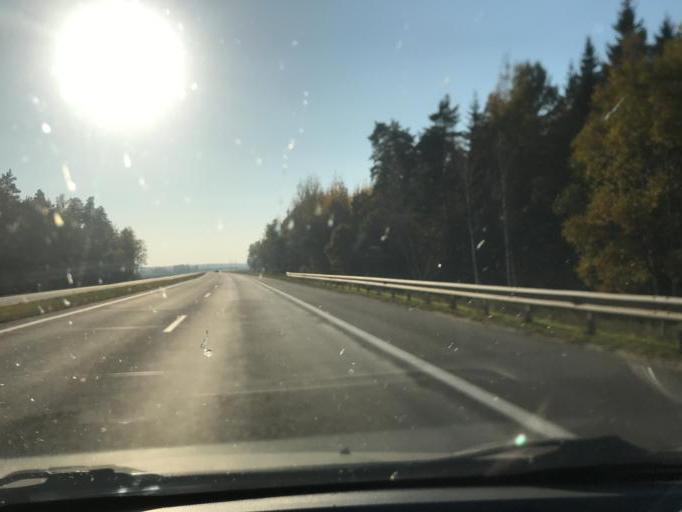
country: BY
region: Minsk
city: Hatava
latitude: 53.7512
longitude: 27.6445
